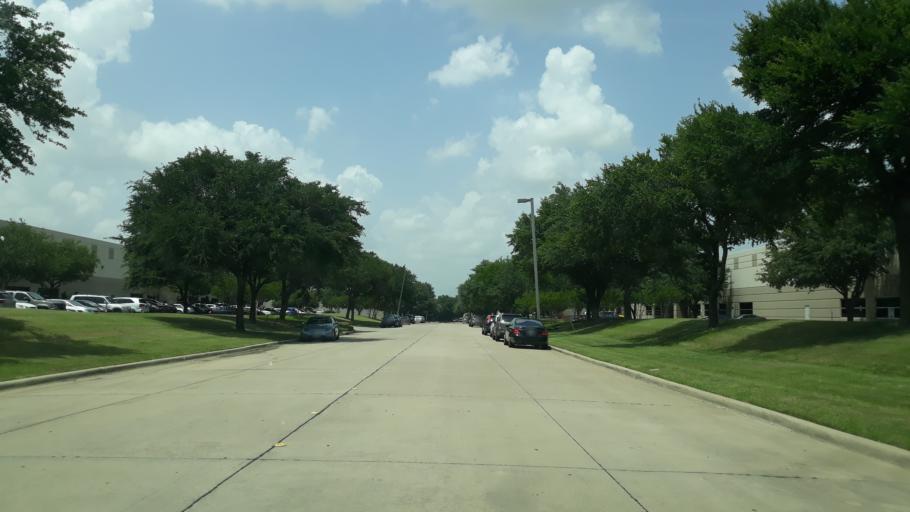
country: US
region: Texas
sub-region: Dallas County
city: Coppell
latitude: 32.9405
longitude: -97.0033
